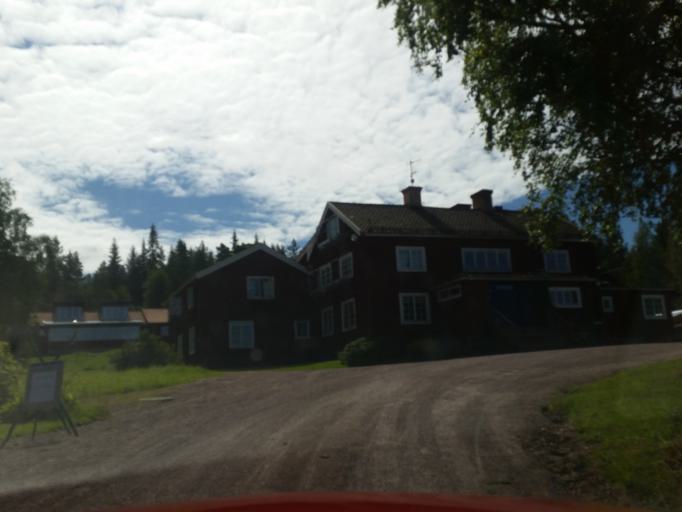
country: SE
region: Dalarna
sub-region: Gagnefs Kommun
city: Gagnef
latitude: 60.6591
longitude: 15.1226
